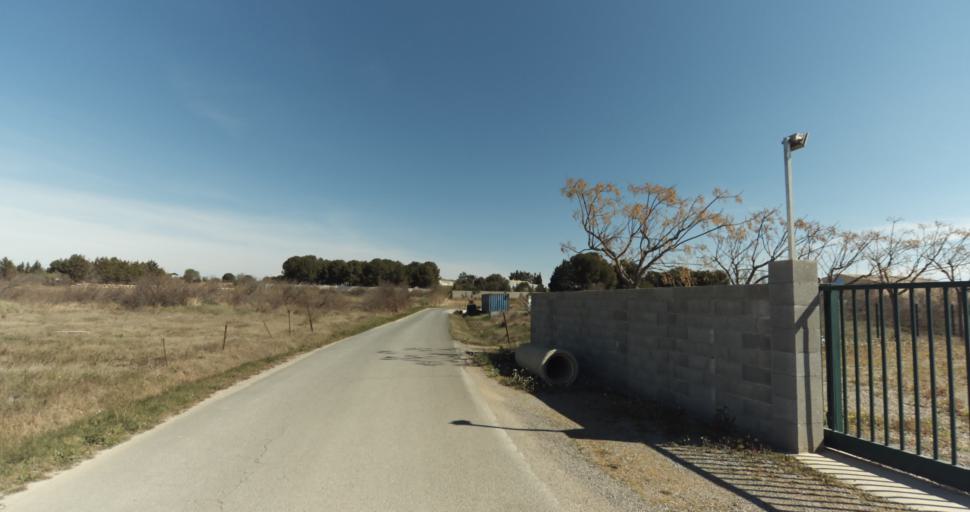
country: FR
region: Languedoc-Roussillon
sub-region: Departement de l'Herault
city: Marseillan
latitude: 43.3656
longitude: 3.5363
